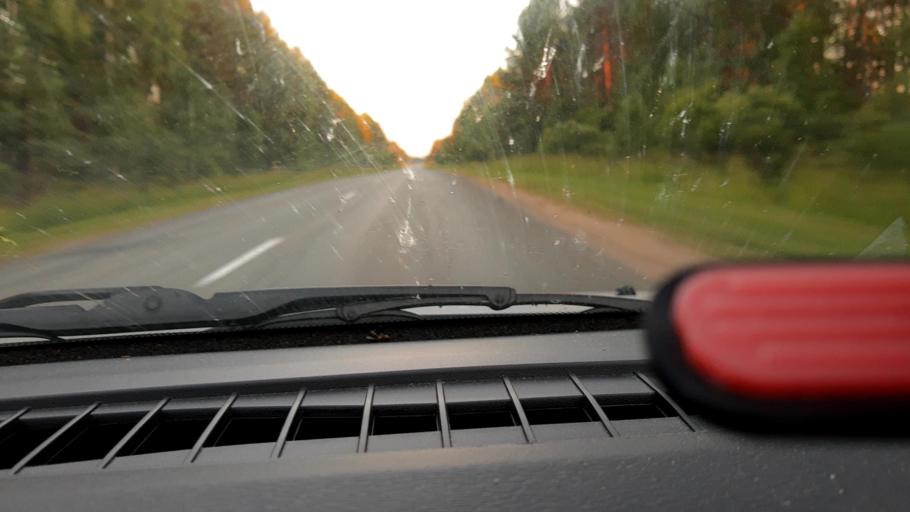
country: RU
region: Nizjnij Novgorod
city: Tonkino
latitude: 57.2888
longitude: 46.4620
